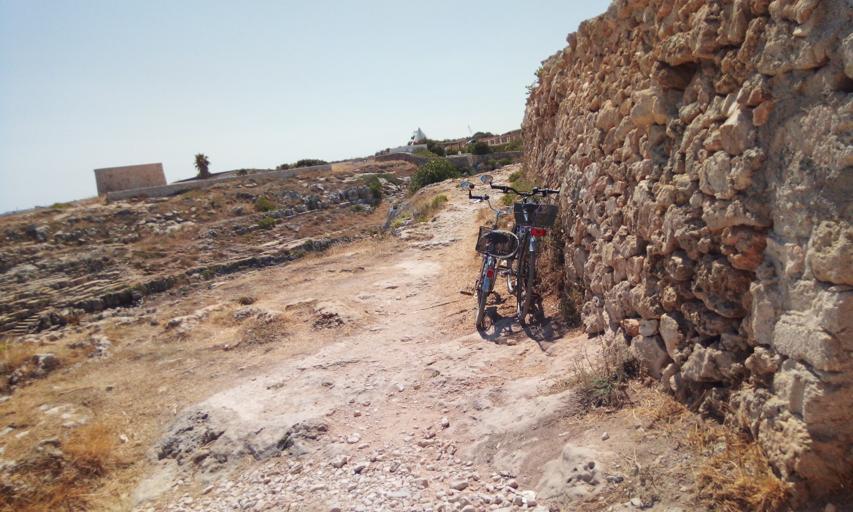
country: IT
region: Apulia
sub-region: Provincia di Bari
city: Polignano a Mare
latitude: 40.9911
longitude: 17.2379
